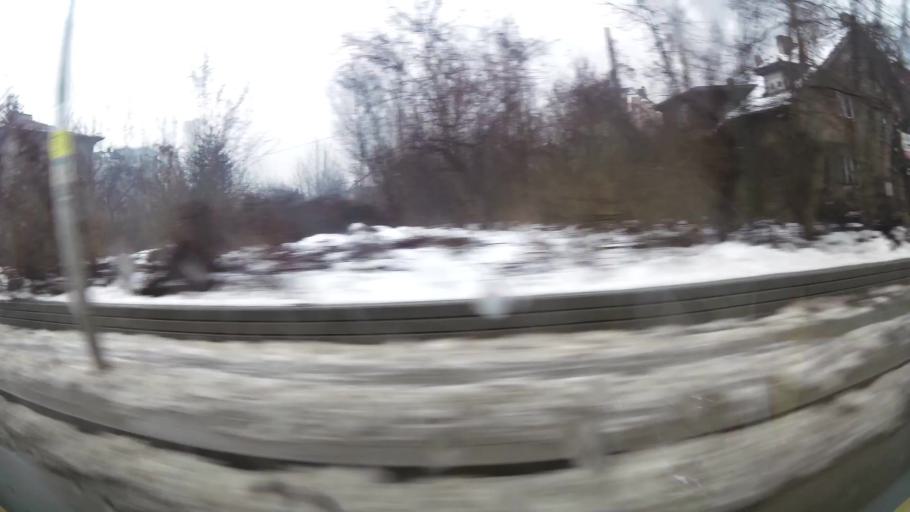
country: BG
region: Sofia-Capital
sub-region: Stolichna Obshtina
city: Sofia
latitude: 42.6749
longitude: 23.2528
